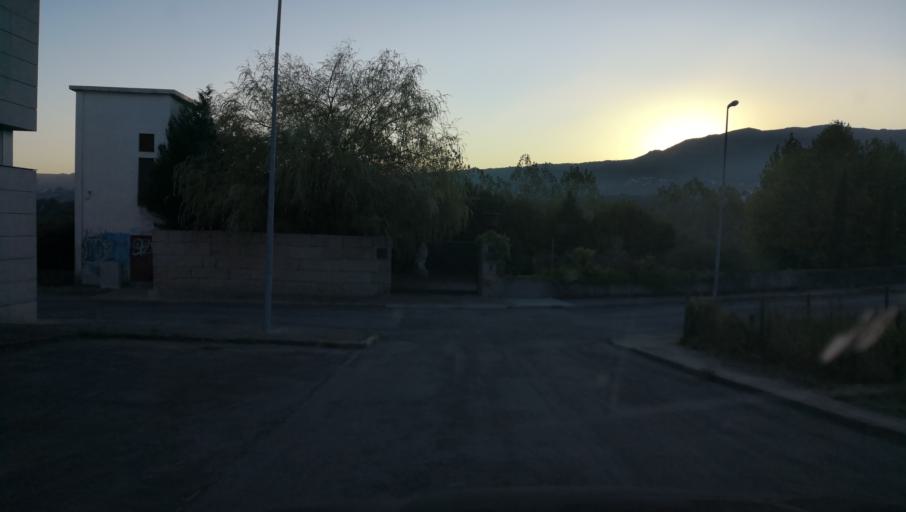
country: PT
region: Vila Real
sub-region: Vila Real
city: Vila Real
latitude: 41.3053
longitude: -7.7659
